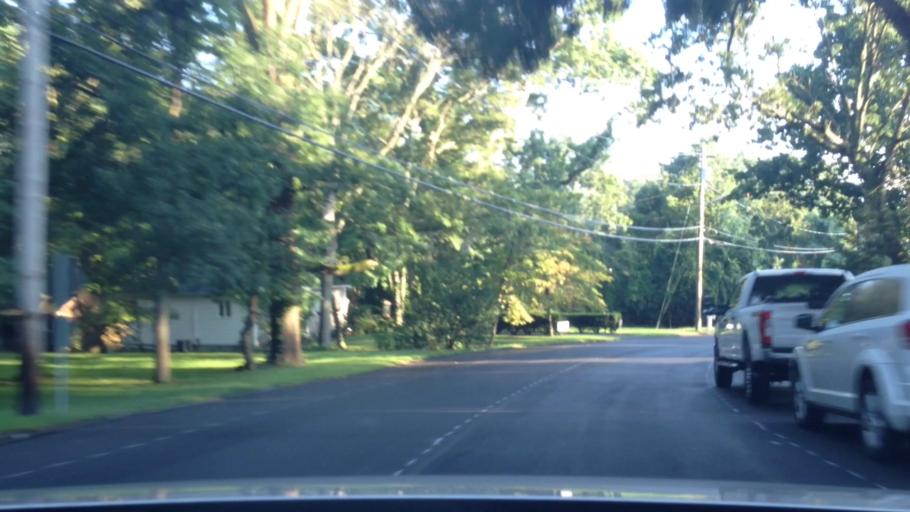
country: US
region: New York
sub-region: Suffolk County
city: Holtsville
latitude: 40.8419
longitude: -73.0588
